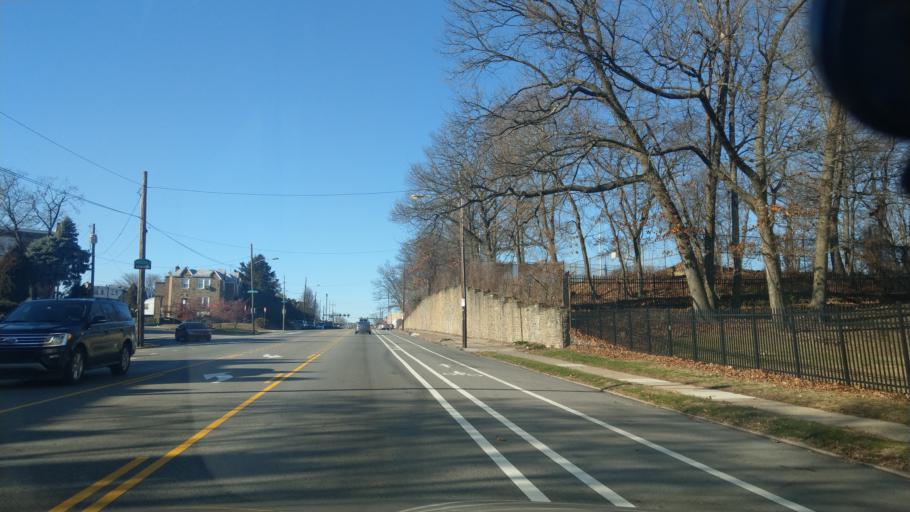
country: US
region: Pennsylvania
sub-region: Montgomery County
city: Wyncote
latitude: 40.0494
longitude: -75.1461
